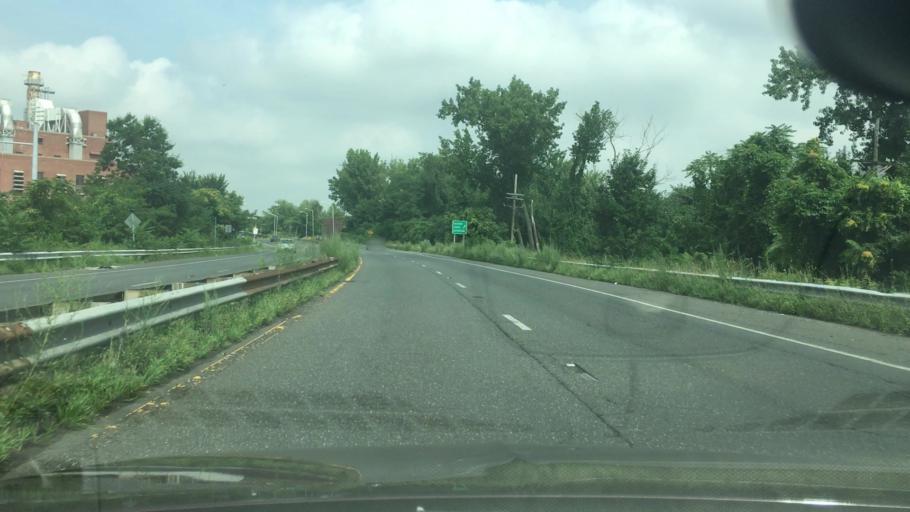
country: US
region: Massachusetts
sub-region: Hampden County
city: Springfield
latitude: 42.0937
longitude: -72.5931
